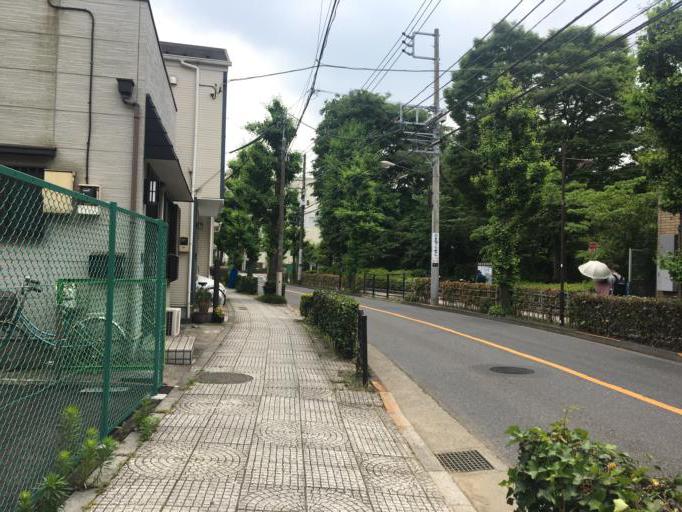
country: JP
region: Saitama
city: Soka
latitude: 35.7369
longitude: 139.7846
